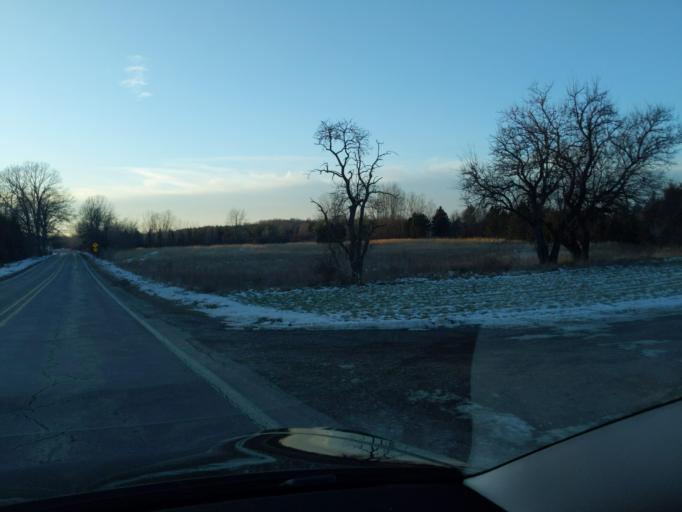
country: US
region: Michigan
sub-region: Ingham County
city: Mason
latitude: 42.5343
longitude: -84.3040
